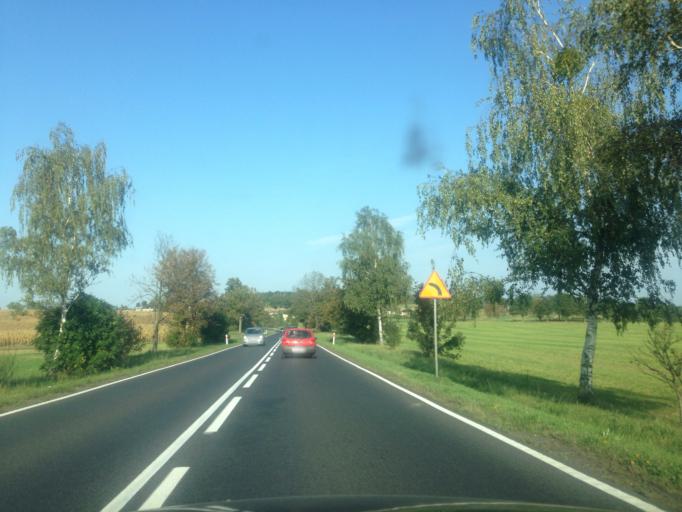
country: PL
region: Kujawsko-Pomorskie
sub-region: Powiat brodnicki
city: Brodnica
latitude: 53.2904
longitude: 19.4948
